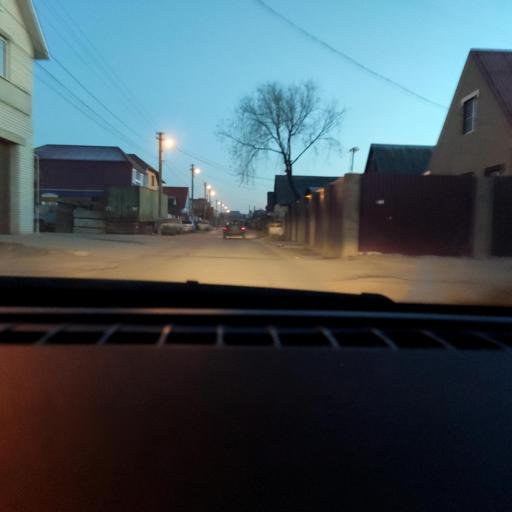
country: RU
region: Voronezj
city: Podgornoye
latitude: 51.7427
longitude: 39.1631
